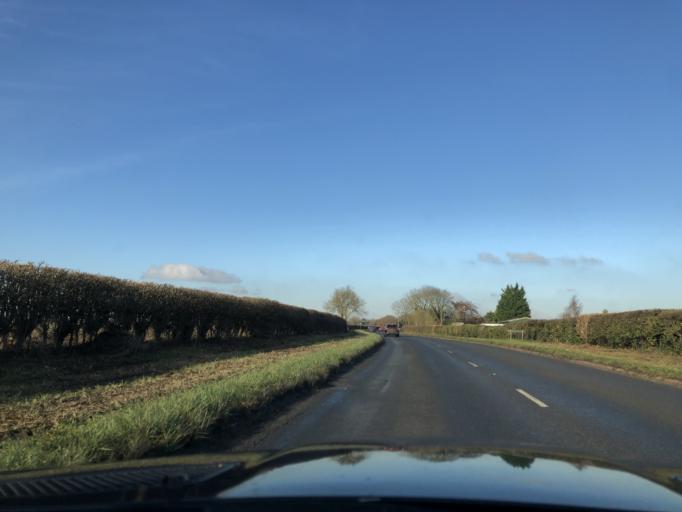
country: GB
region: England
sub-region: Buckinghamshire
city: High Wycombe
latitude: 51.6042
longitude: -0.7701
